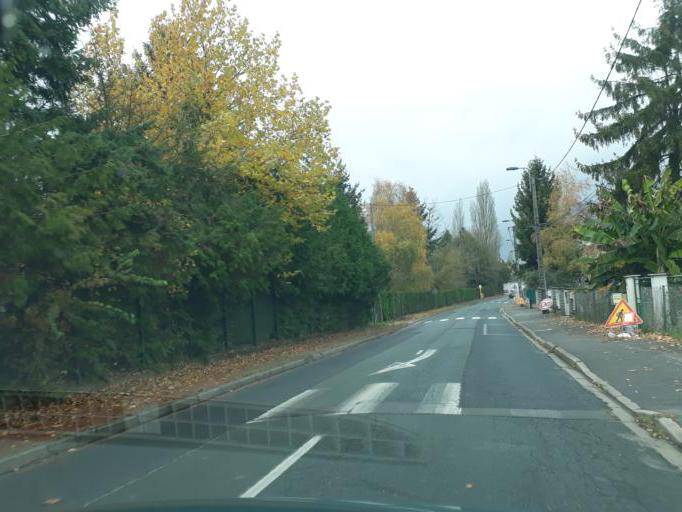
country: FR
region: Centre
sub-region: Departement du Loiret
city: Saran
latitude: 47.9433
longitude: 1.8851
